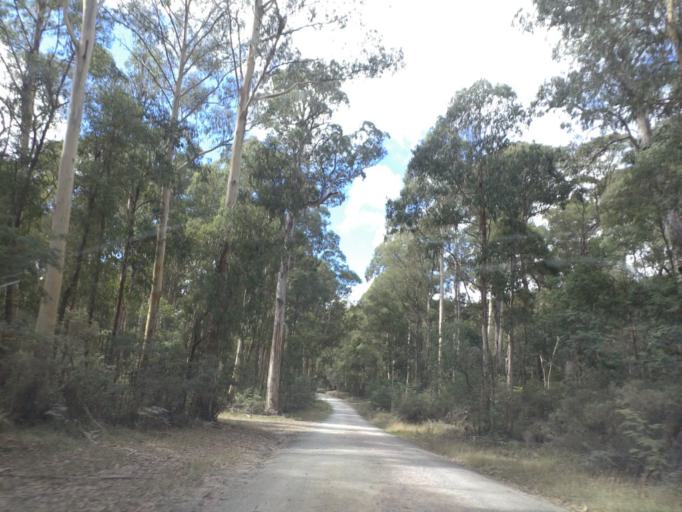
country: AU
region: Victoria
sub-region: Yarra Ranges
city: Millgrove
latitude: -37.5413
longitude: 145.9282
